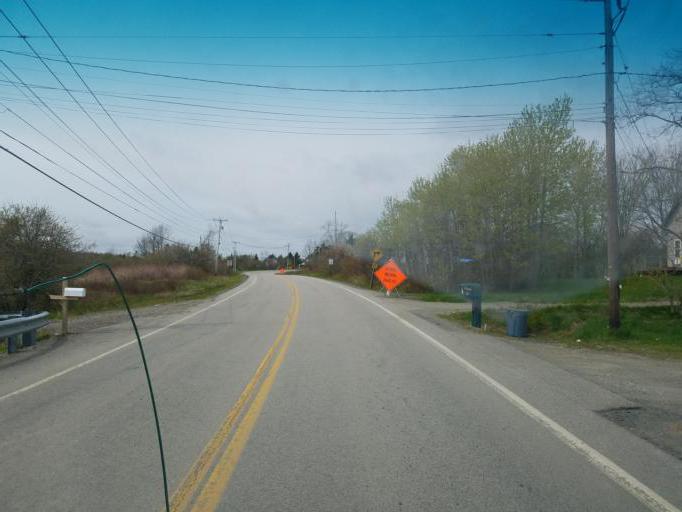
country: US
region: Maine
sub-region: Washington County
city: Eastport
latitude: 44.7896
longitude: -67.1714
